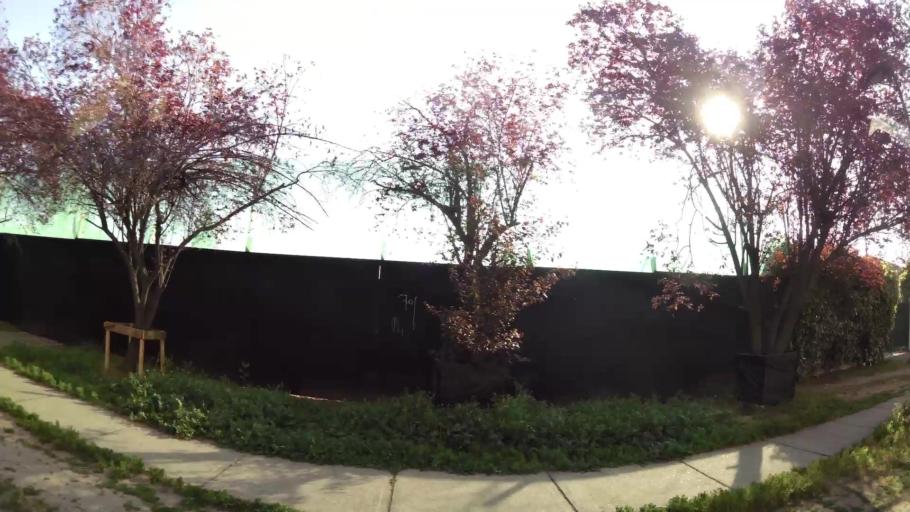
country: CL
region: Santiago Metropolitan
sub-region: Provincia de Santiago
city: Villa Presidente Frei, Nunoa, Santiago, Chile
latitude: -33.3525
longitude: -70.5133
